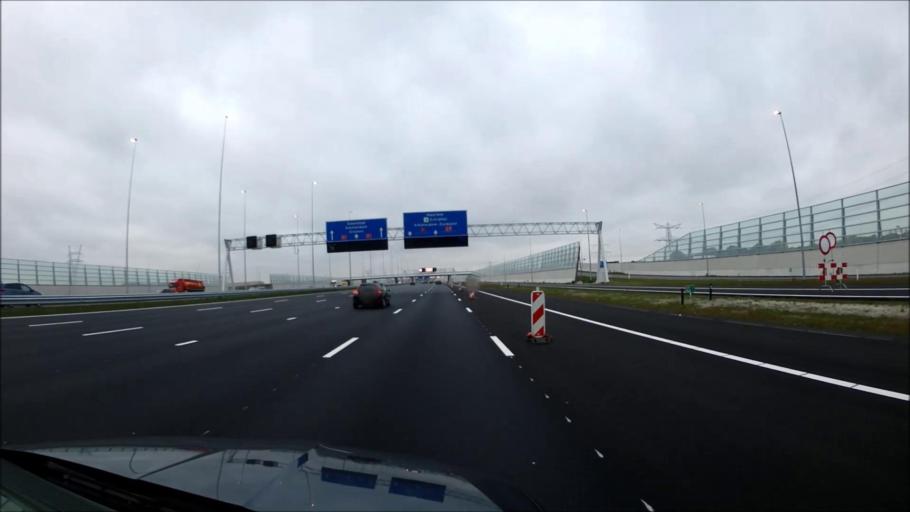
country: NL
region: North Holland
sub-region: Gemeente Weesp
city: Weesp
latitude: 52.3274
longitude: 5.0516
